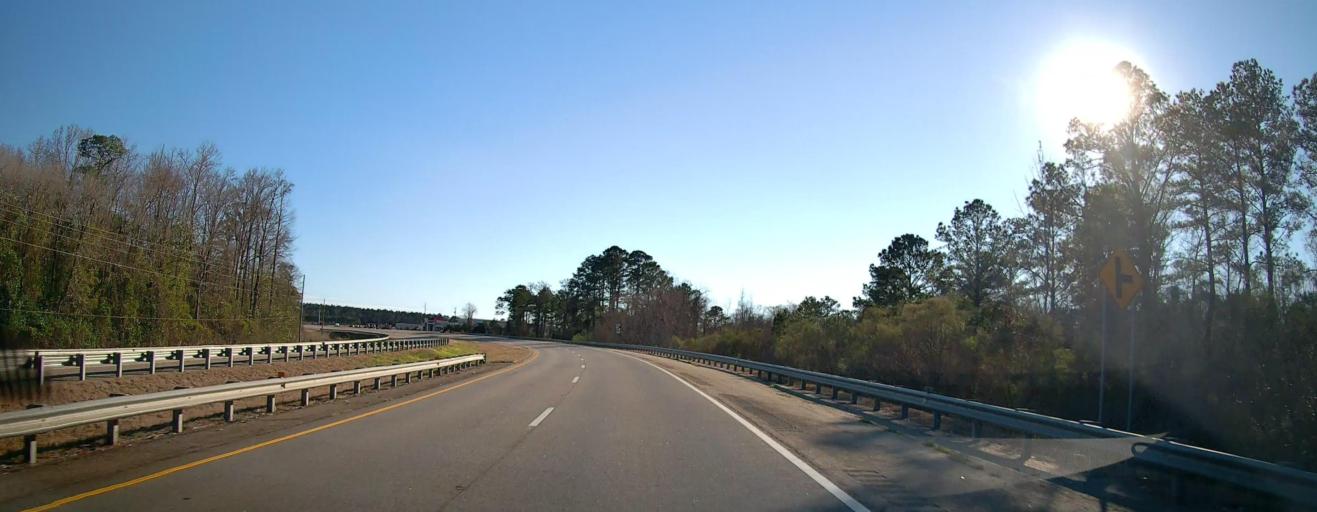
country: US
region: Georgia
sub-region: Sumter County
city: Americus
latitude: 31.9275
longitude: -84.2652
